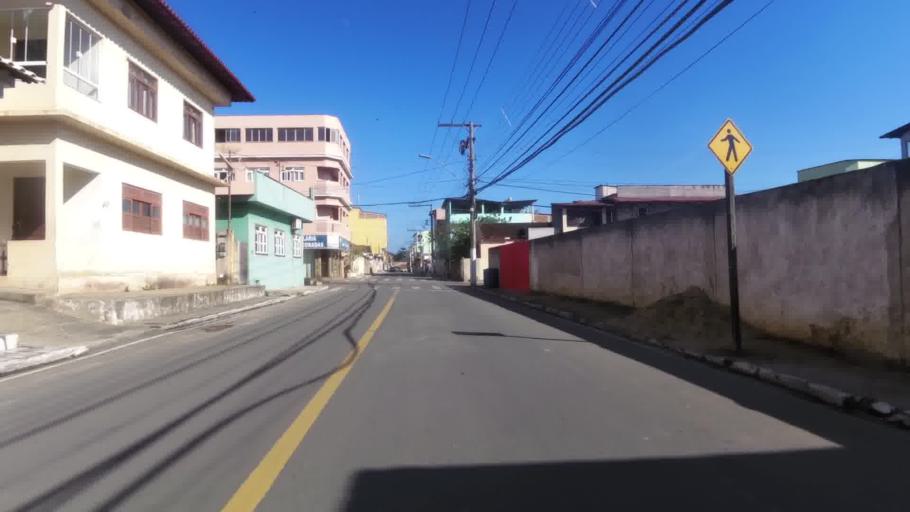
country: BR
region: Espirito Santo
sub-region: Piuma
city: Piuma
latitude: -20.8064
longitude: -40.6459
